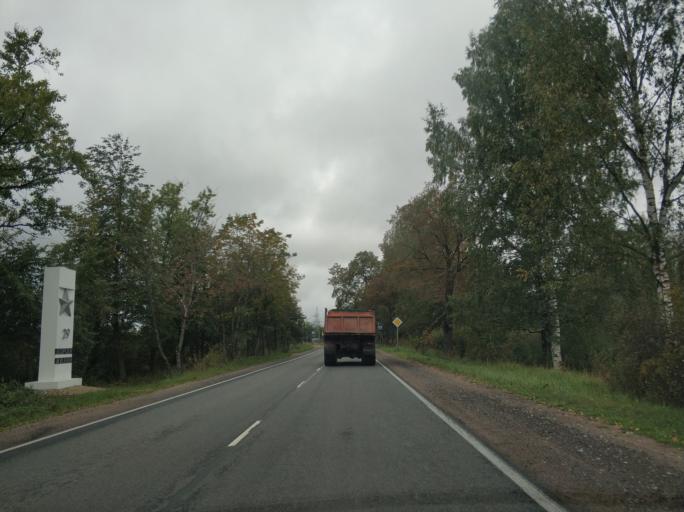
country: RU
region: Leningrad
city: Borisova Griva
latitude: 60.0835
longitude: 30.8992
